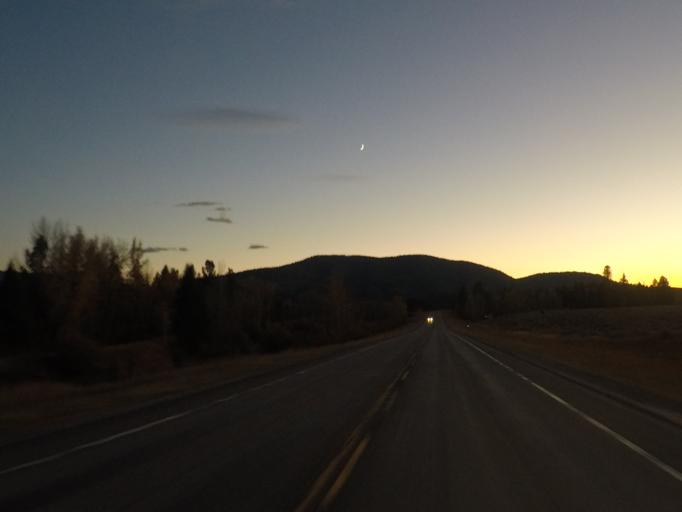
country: US
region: Montana
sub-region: Missoula County
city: Seeley Lake
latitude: 47.0386
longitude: -113.2260
